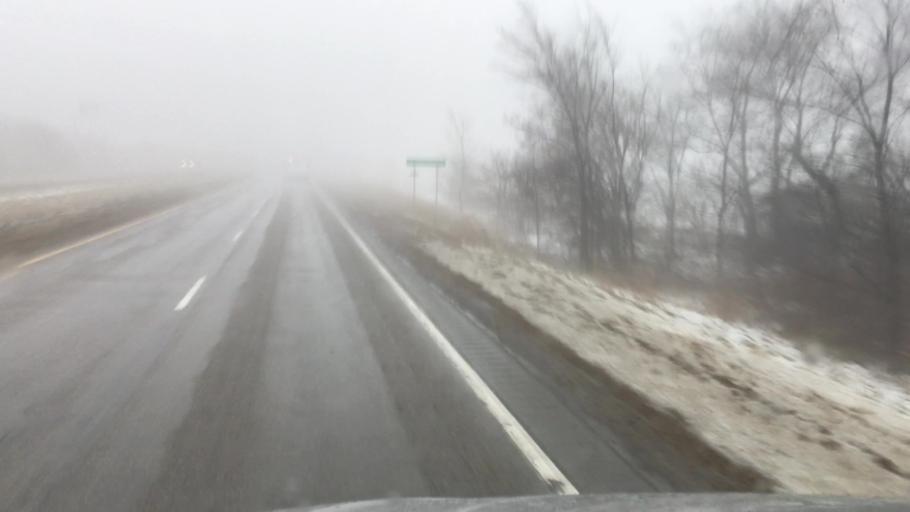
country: US
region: Indiana
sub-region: Newton County
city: Roselawn
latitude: 41.1264
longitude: -87.4517
